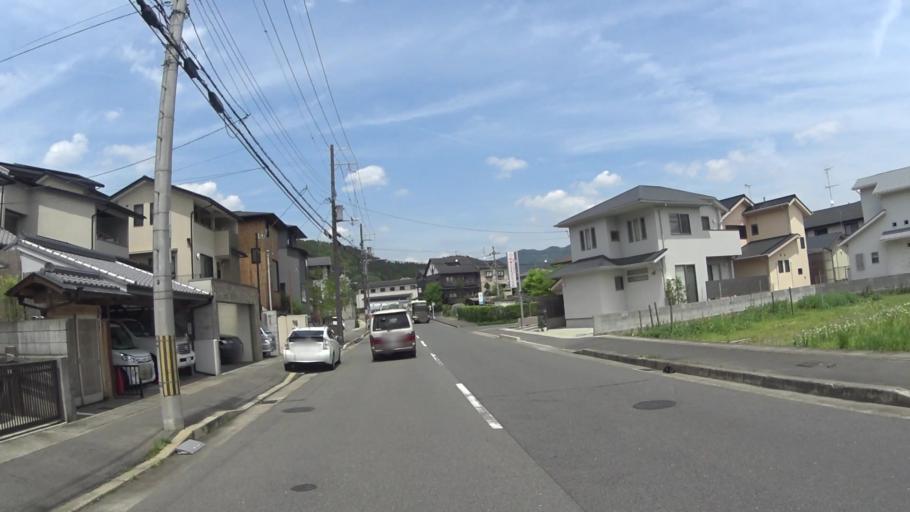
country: JP
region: Kyoto
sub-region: Kyoto-shi
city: Kamigyo-ku
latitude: 35.0676
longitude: 135.7766
